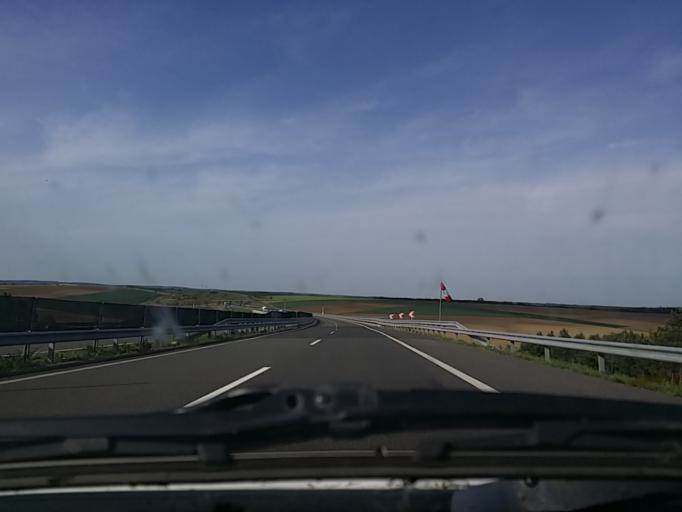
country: HU
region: Baranya
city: Lanycsok
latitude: 46.0709
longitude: 18.5881
